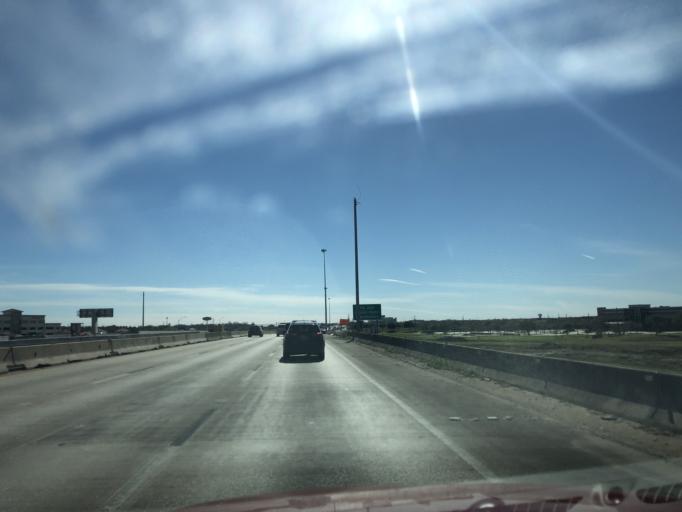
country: US
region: Texas
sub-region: Brazoria County
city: Brookside Village
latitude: 29.5805
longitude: -95.3865
